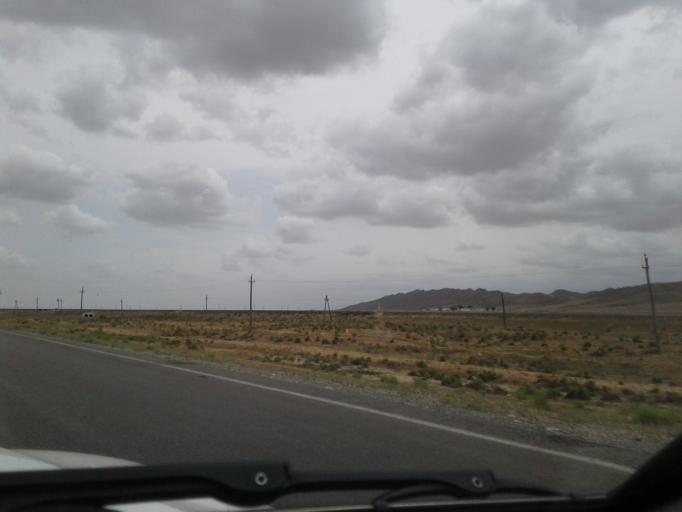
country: IR
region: Razavi Khorasan
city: Dargaz
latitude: 37.5939
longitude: 59.2180
